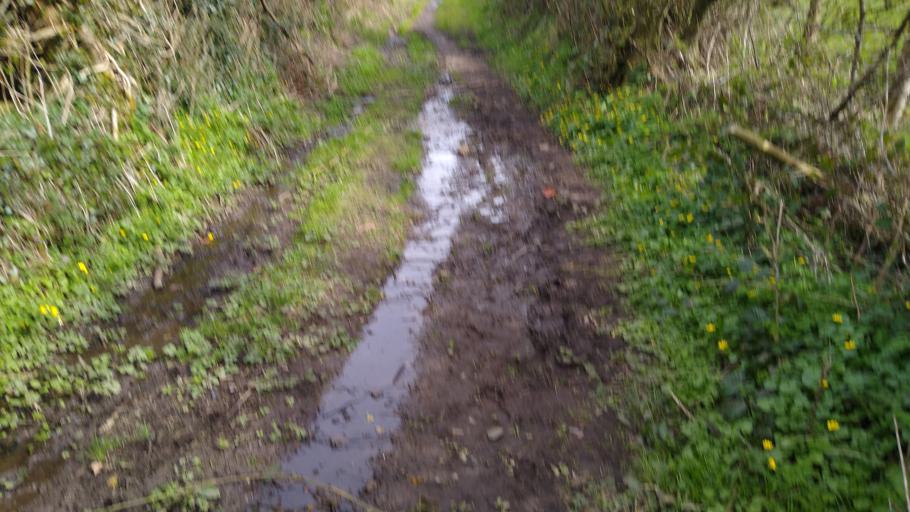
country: GB
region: England
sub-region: Cumbria
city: Dearham
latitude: 54.6732
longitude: -3.4277
